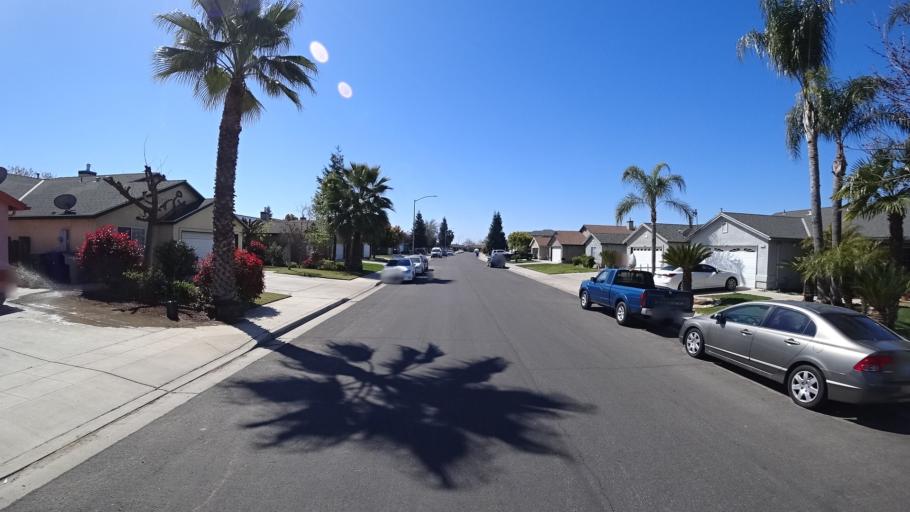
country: US
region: California
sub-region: Fresno County
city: Biola
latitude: 36.8143
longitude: -119.9046
